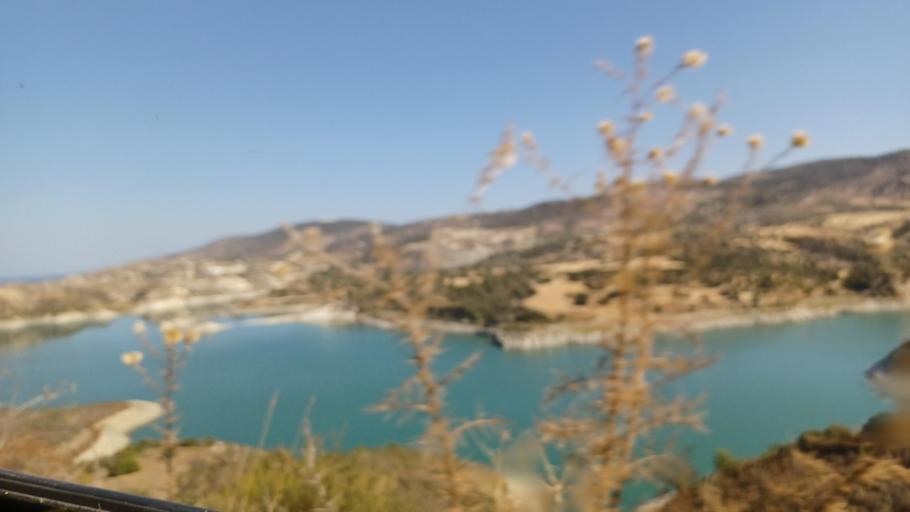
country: CY
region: Pafos
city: Polis
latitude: 34.9603
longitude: 32.4698
